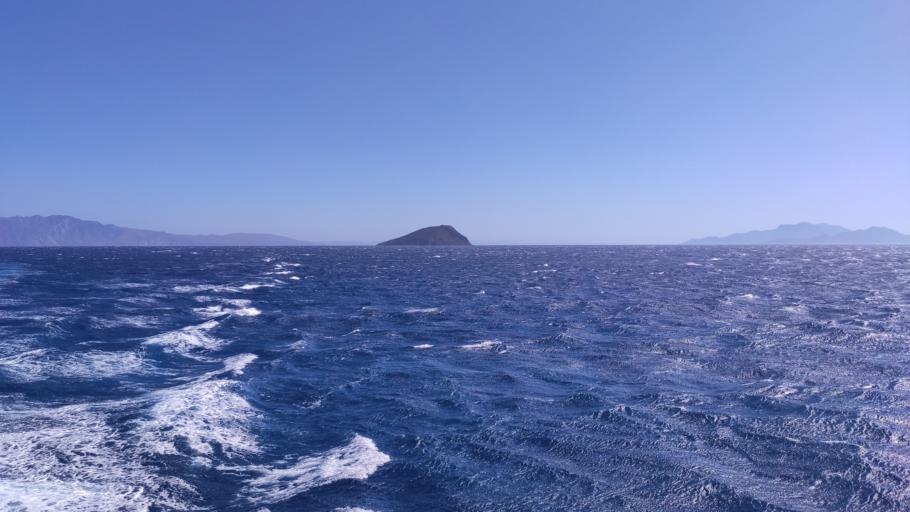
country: GR
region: South Aegean
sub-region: Nomos Dodekanisou
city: Mandraki
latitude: 36.6549
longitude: 27.1444
